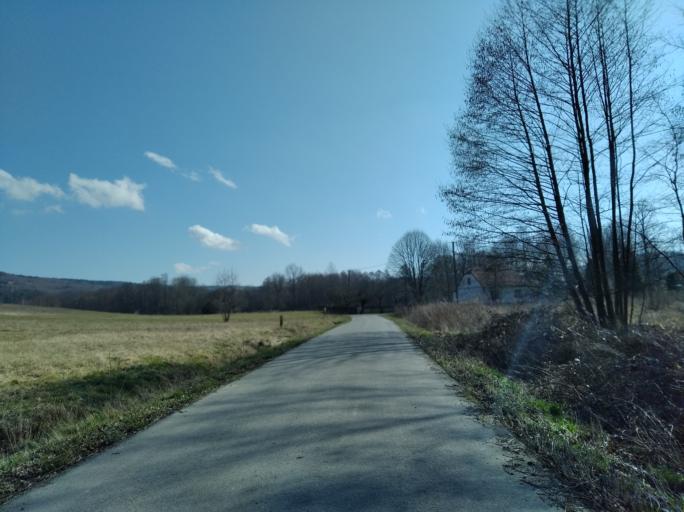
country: PL
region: Subcarpathian Voivodeship
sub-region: Powiat strzyzowski
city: Wysoka Strzyzowska
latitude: 49.8281
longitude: 21.7444
